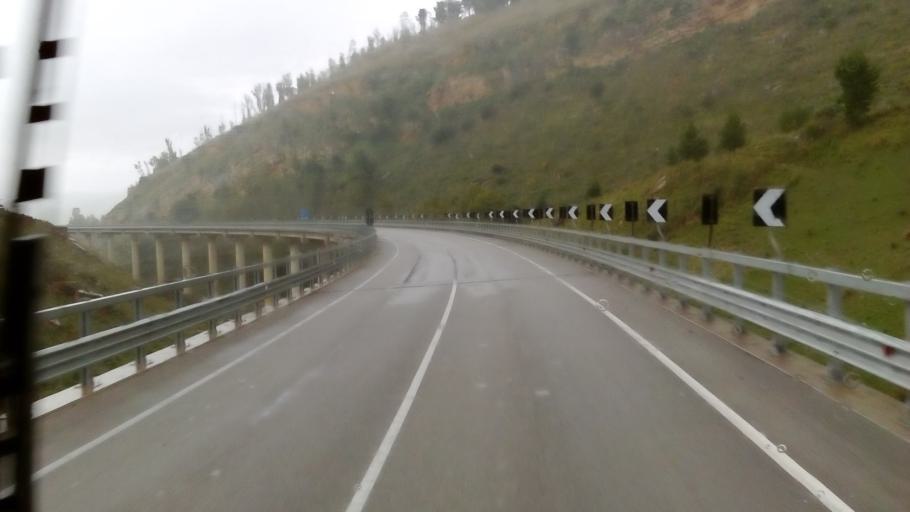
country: IT
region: Sicily
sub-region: Enna
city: Pietraperzia
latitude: 37.5016
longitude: 14.1409
